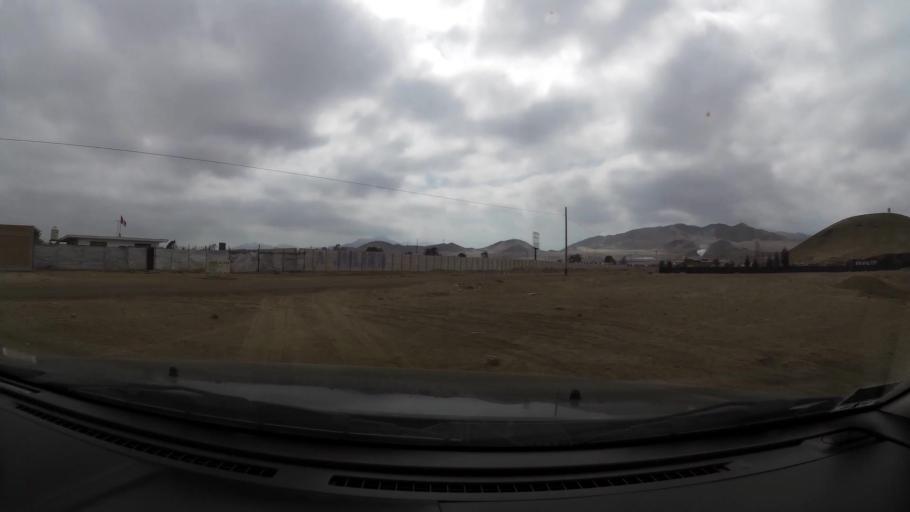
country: PE
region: Lima
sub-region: Provincia de Canete
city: Chilca
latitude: -12.5235
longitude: -76.7280
